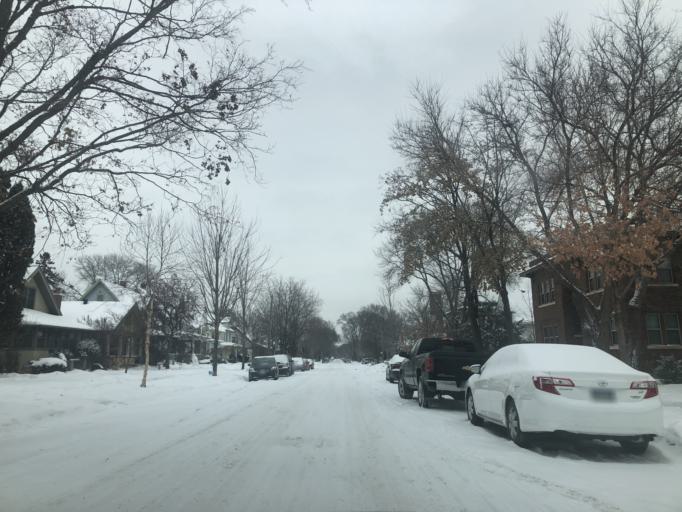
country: US
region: Minnesota
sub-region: Hennepin County
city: Richfield
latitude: 44.9311
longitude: -93.2831
